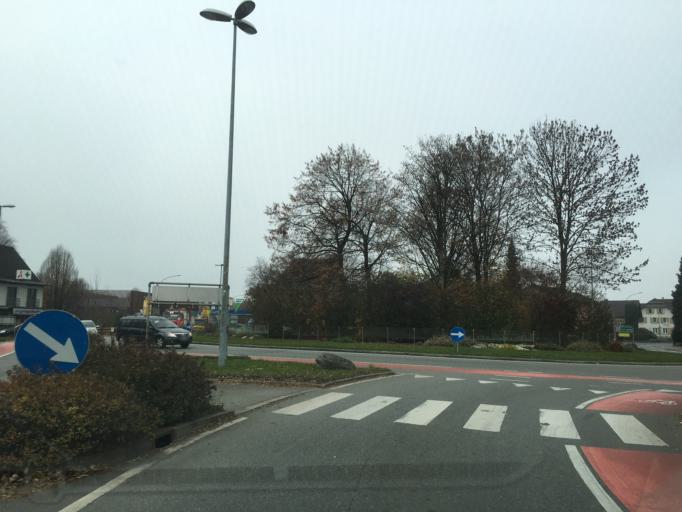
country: AT
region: Vorarlberg
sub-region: Politischer Bezirk Dornbirn
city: Lustenau
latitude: 47.4191
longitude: 9.6607
